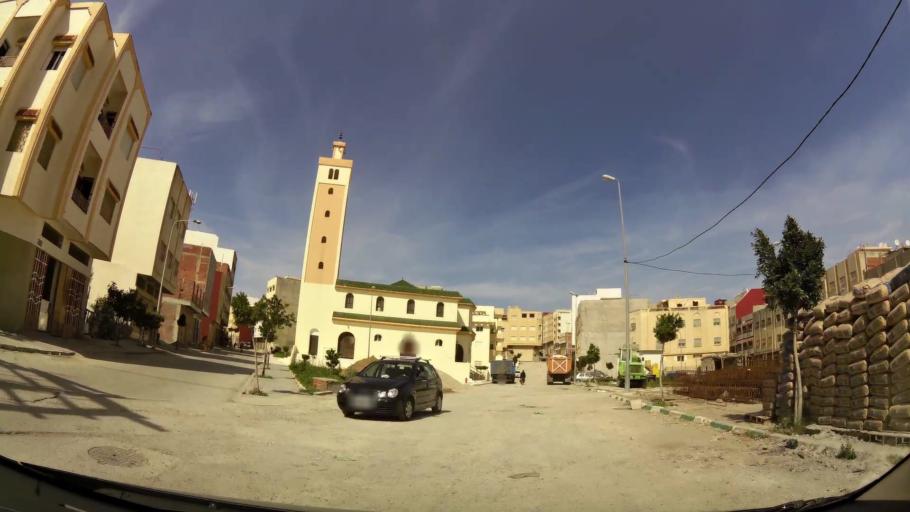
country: MA
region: Tanger-Tetouan
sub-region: Tanger-Assilah
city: Tangier
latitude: 35.7328
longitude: -5.8039
